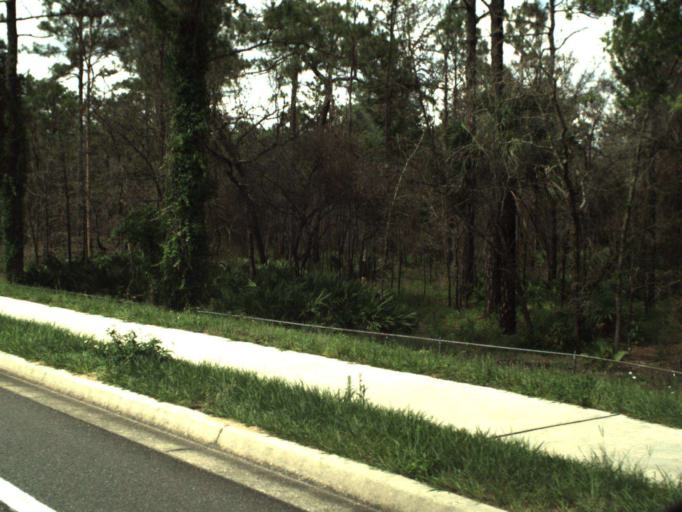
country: US
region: Florida
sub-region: Marion County
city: Ocala
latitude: 29.2067
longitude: -82.0548
